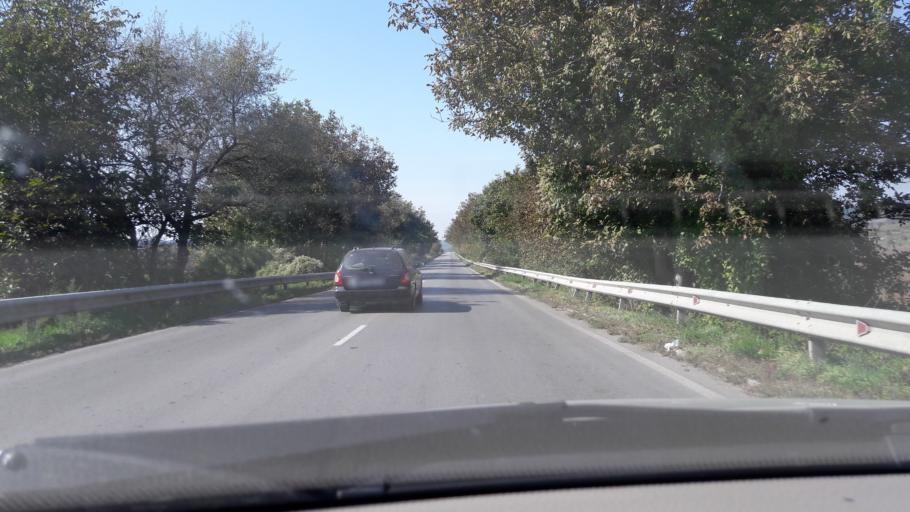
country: BG
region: Razgrad
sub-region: Obshtina Razgrad
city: Razgrad
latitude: 43.5457
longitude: 26.4930
